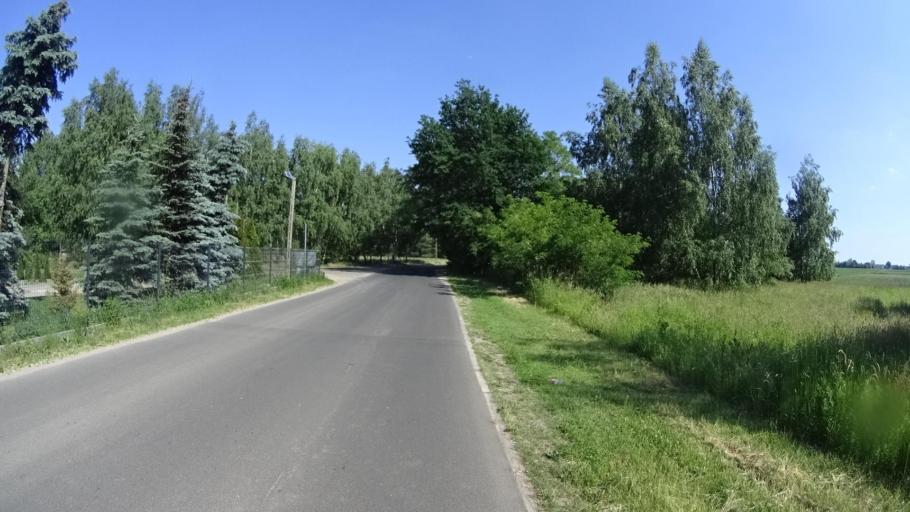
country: PL
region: Masovian Voivodeship
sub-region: Powiat warszawski zachodni
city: Blonie
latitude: 52.1646
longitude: 20.6359
